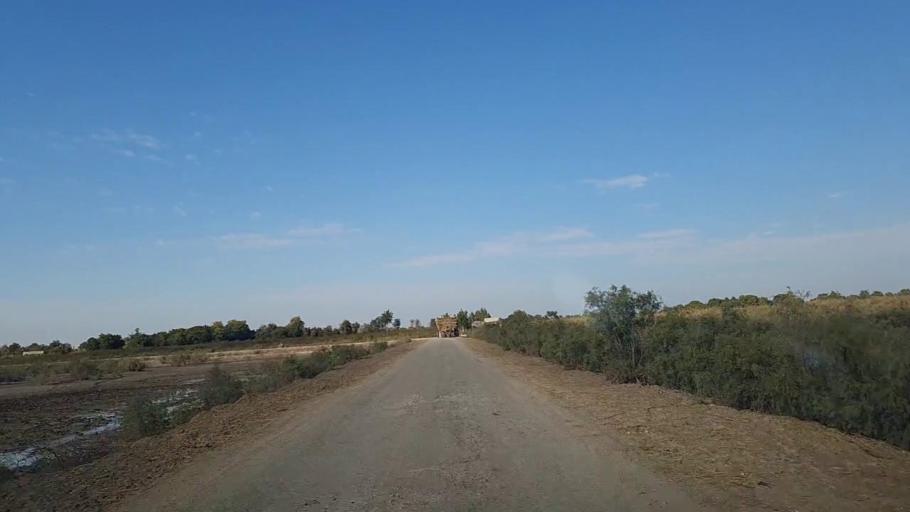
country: PK
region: Sindh
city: Khadro
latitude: 26.3007
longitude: 68.8202
